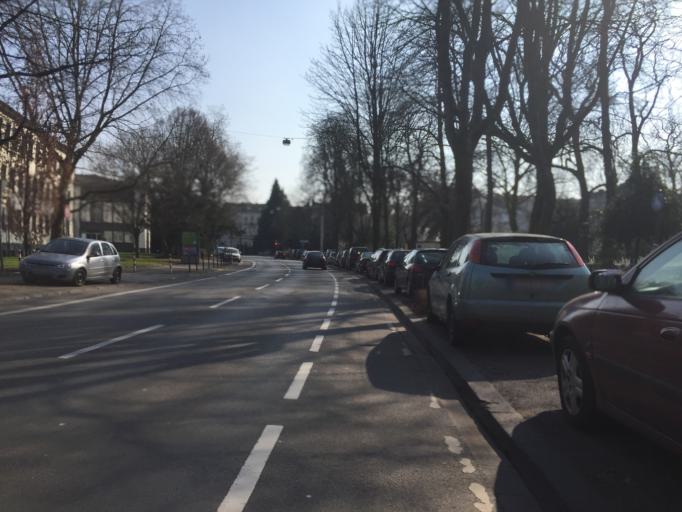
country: DE
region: North Rhine-Westphalia
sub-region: Regierungsbezirk Koln
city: Bonn
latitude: 50.7322
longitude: 7.0883
